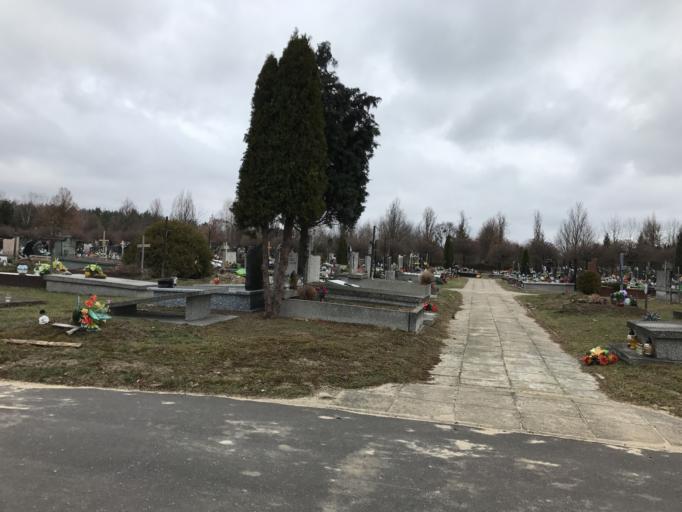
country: PL
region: Masovian Voivodeship
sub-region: Powiat warszawski zachodni
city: Lomianki
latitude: 52.3037
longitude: 20.8876
